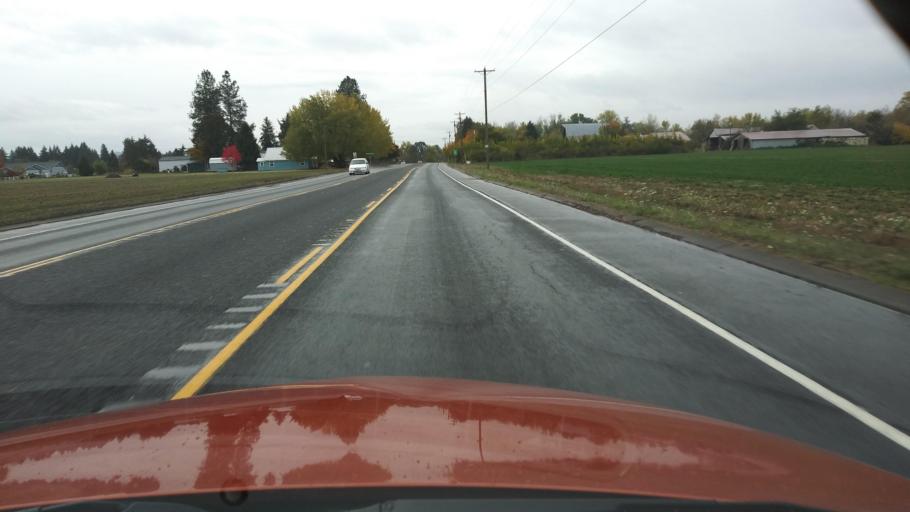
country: US
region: Oregon
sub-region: Washington County
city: Cornelius
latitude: 45.5598
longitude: -123.0573
